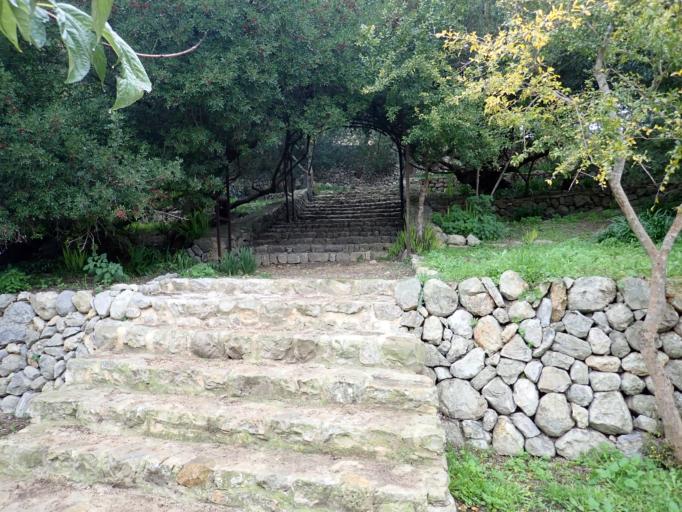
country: ES
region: Balearic Islands
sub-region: Illes Balears
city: Sant Joan
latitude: 39.5861
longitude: 3.0642
